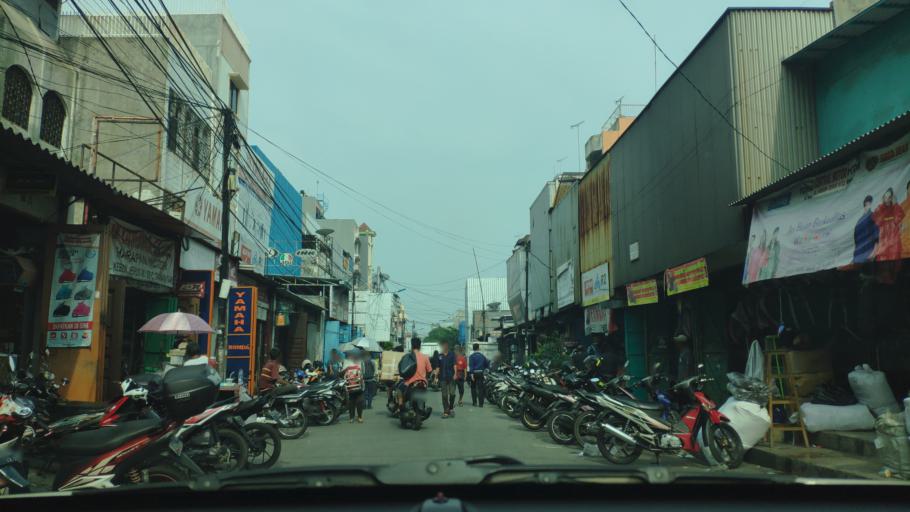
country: ID
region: Jakarta Raya
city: Jakarta
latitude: -6.1585
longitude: 106.8201
